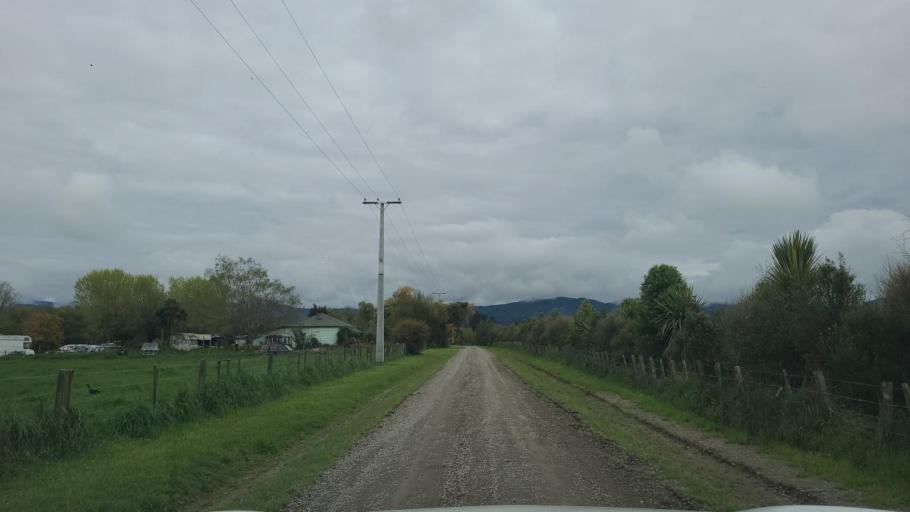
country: NZ
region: Wellington
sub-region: Masterton District
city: Masterton
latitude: -41.0497
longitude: 175.4964
